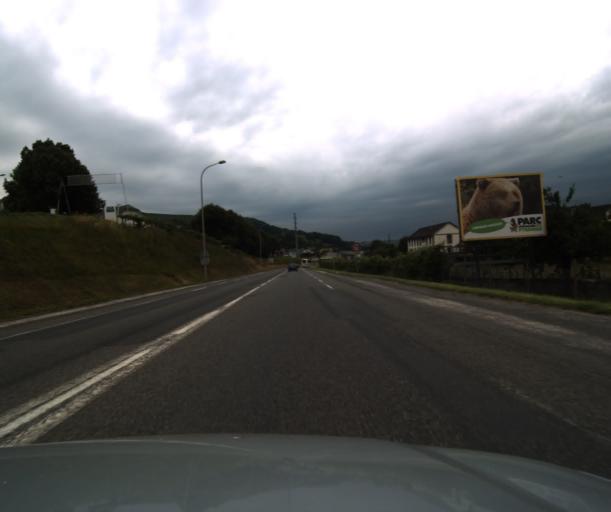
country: FR
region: Midi-Pyrenees
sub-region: Departement des Hautes-Pyrenees
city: Lourdes
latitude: 43.1042
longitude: -0.0342
